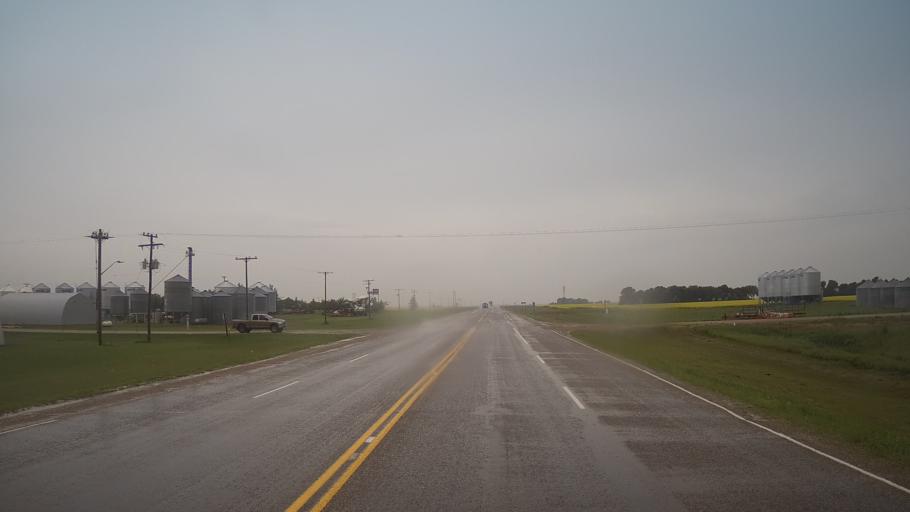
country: CA
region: Saskatchewan
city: Wilkie
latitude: 52.2020
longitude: -108.4539
